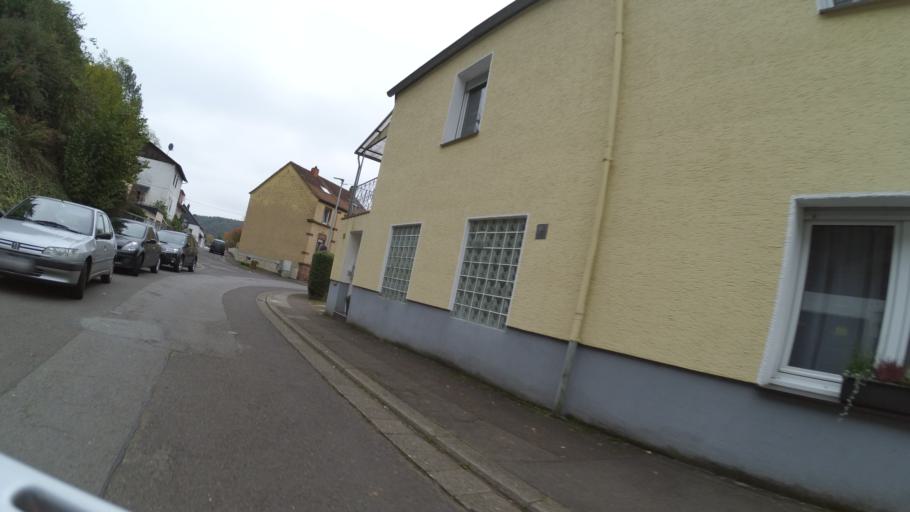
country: DE
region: Saarland
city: Blieskastel
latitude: 49.2661
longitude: 7.2791
